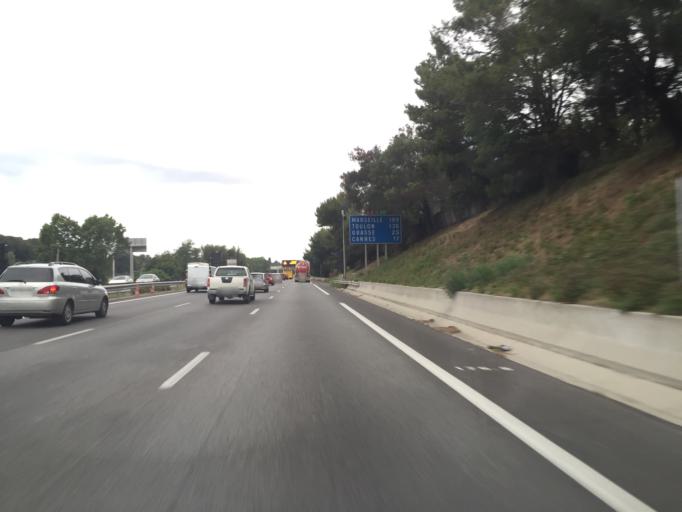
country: FR
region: Provence-Alpes-Cote d'Azur
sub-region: Departement des Alpes-Maritimes
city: Biot
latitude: 43.6265
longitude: 7.1161
